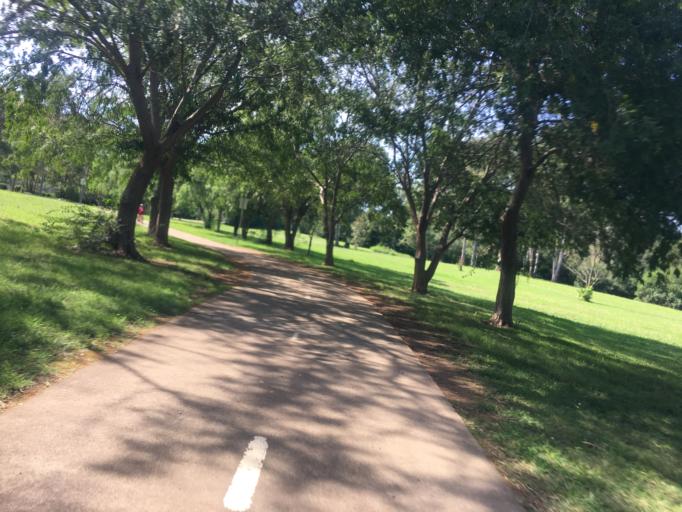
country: AU
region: New South Wales
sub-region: Camden
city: Camden South
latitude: -34.0781
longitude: 150.7006
